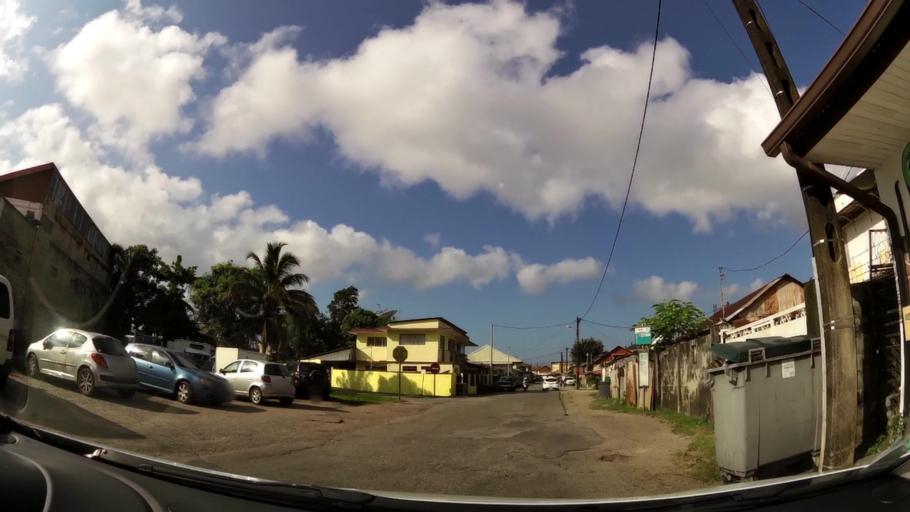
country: GF
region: Guyane
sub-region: Guyane
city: Cayenne
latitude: 4.9332
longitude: -52.3196
